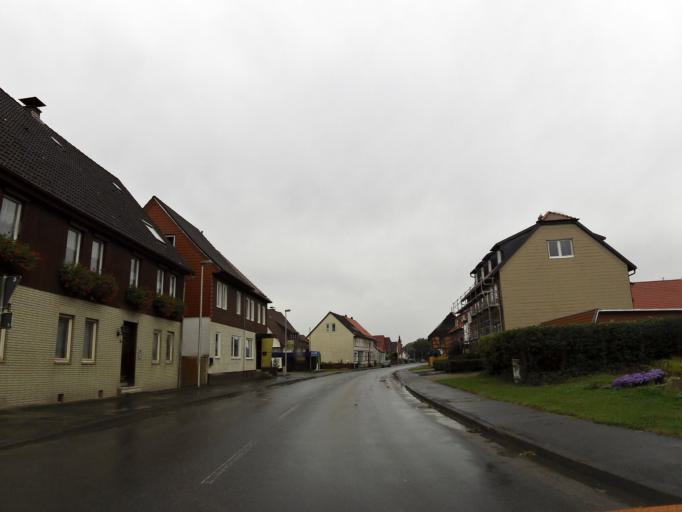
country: DE
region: Lower Saxony
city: Herzberg am Harz
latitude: 51.6303
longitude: 10.3718
